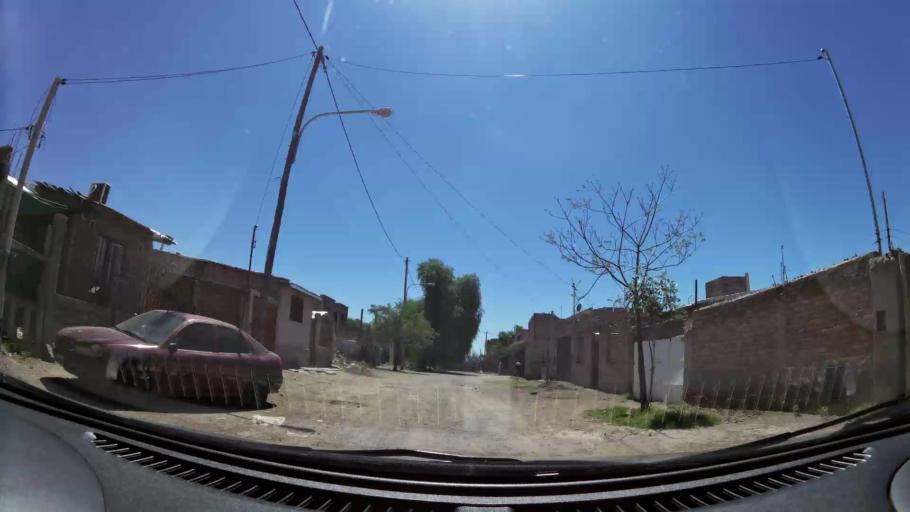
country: AR
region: Mendoza
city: Las Heras
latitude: -32.8518
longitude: -68.8670
